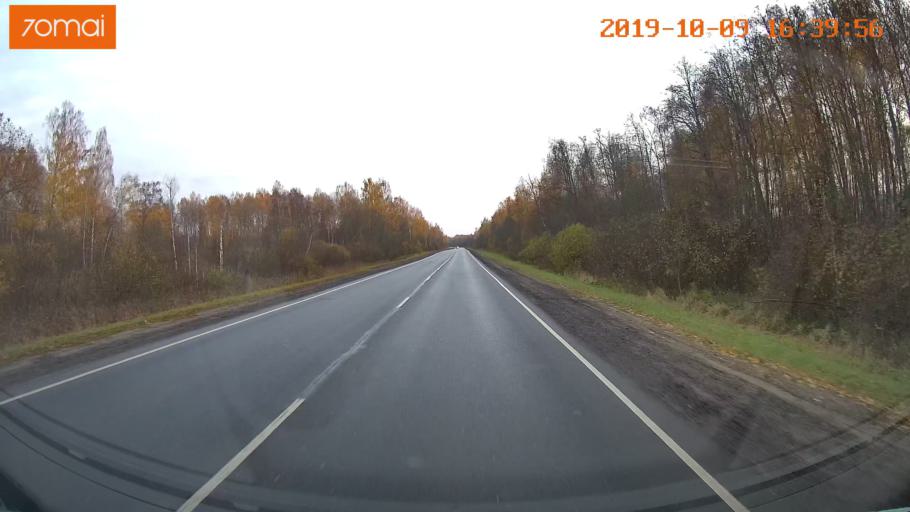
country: RU
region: Kostroma
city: Volgorechensk
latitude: 57.4909
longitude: 41.0543
